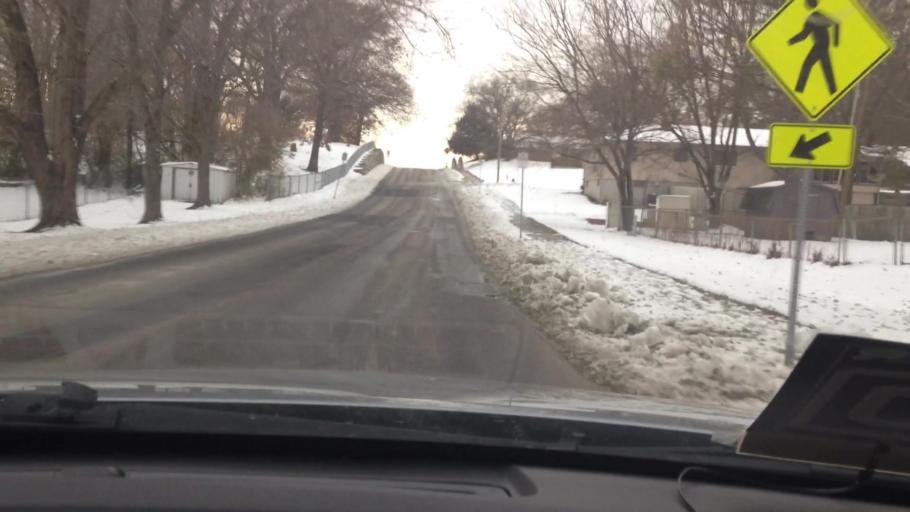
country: US
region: Kansas
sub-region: Leavenworth County
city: Leavenworth
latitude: 39.2885
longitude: -94.9372
